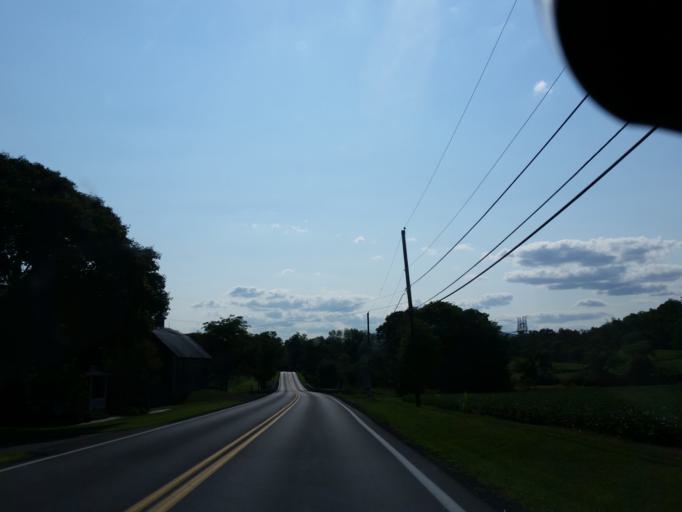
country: US
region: Pennsylvania
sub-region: Union County
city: Linntown
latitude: 41.0158
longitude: -76.9456
